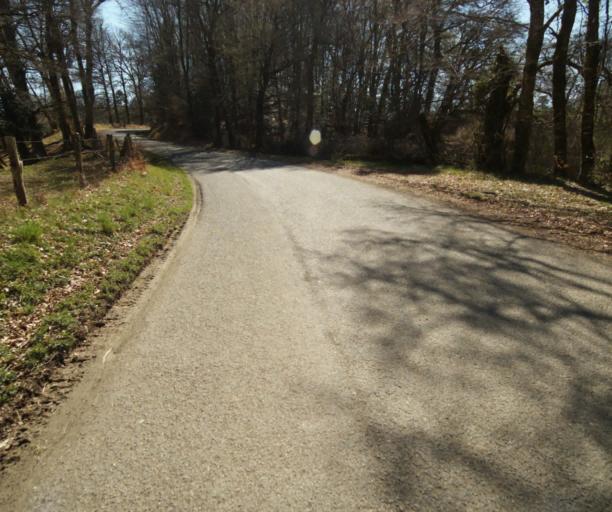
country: FR
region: Limousin
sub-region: Departement de la Correze
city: Saint-Clement
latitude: 45.2987
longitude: 1.7041
